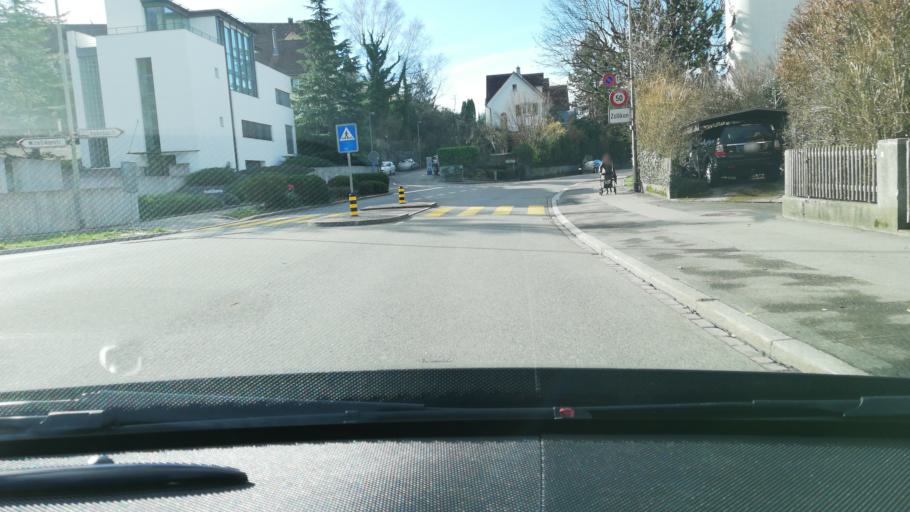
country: CH
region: Zurich
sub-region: Bezirk Zuerich
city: Zuerich (Kreis 8) / Weinegg
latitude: 47.3490
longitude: 8.5778
